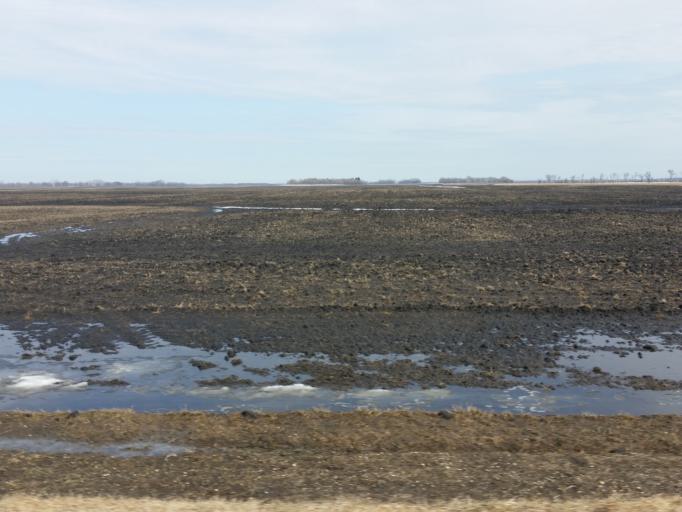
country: US
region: North Dakota
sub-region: Walsh County
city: Grafton
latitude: 48.4275
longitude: -97.2558
